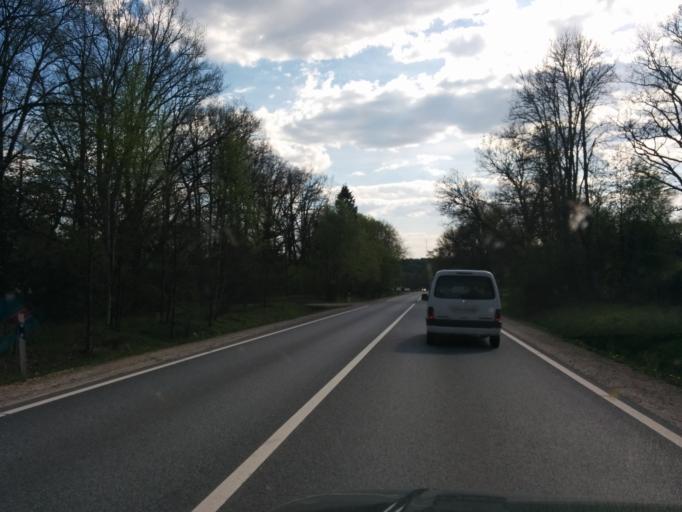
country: LV
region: Seja
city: Loja
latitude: 57.1347
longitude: 24.6658
